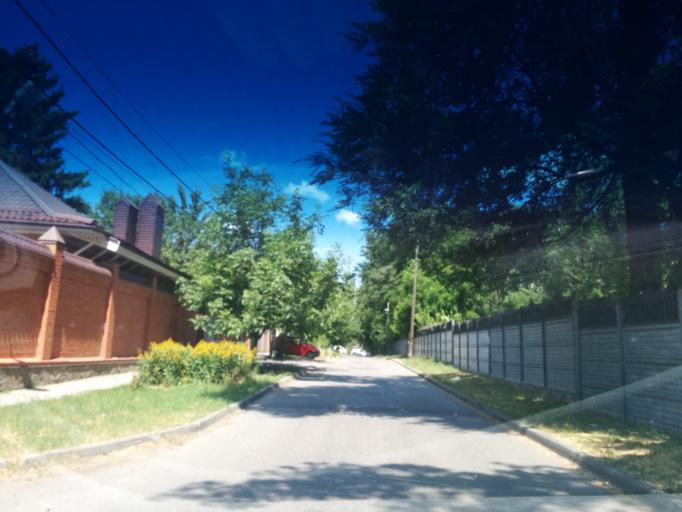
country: RU
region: Rostov
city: Rostov-na-Donu
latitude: 47.2361
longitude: 39.7484
